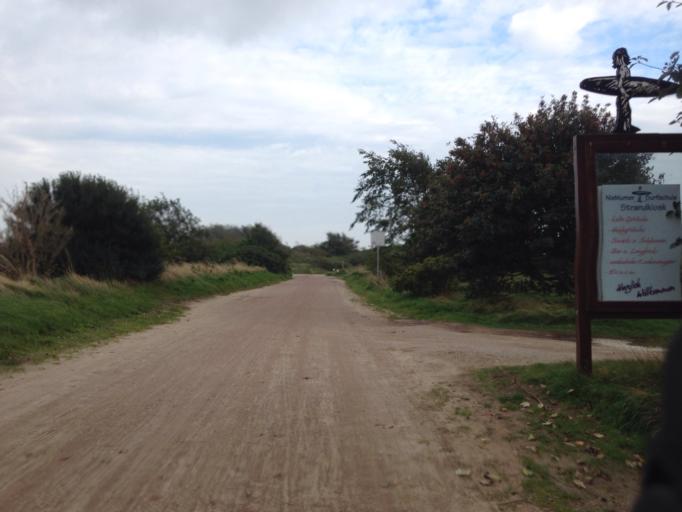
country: DE
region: Schleswig-Holstein
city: Nieblum
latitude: 54.6821
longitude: 8.4837
